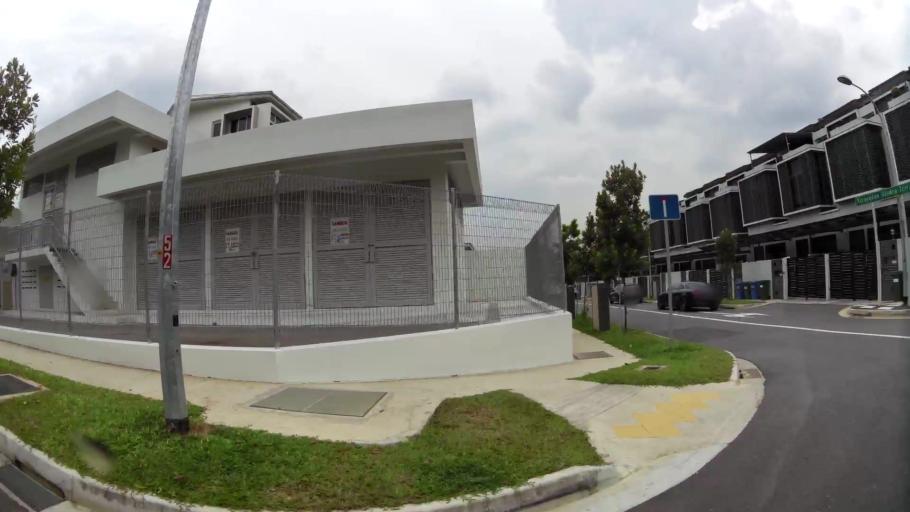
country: SG
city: Singapore
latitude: 1.3657
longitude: 103.8606
